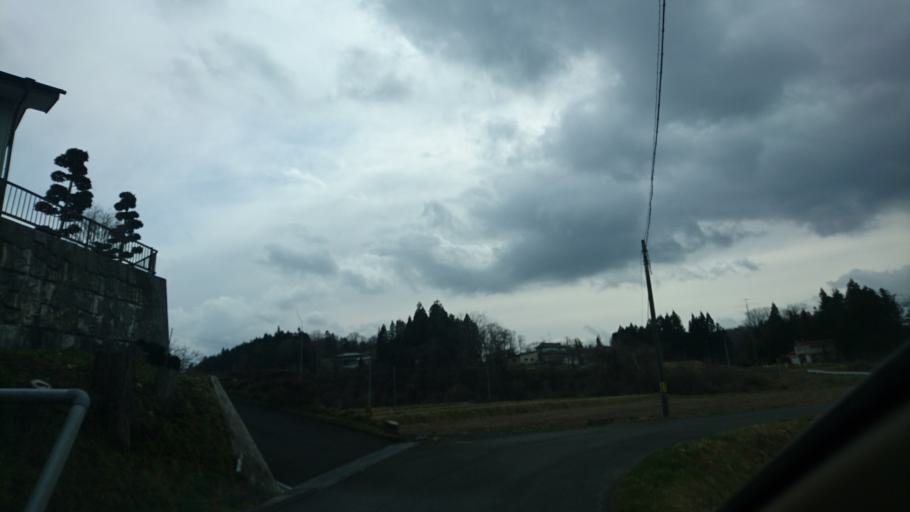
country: JP
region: Iwate
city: Ichinoseki
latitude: 38.8994
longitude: 141.1735
